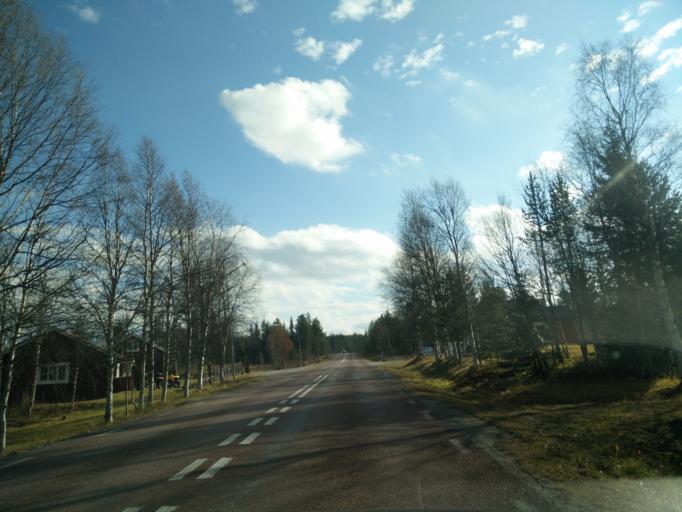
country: NO
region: Hedmark
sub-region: Engerdal
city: Engerdal
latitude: 62.5051
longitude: 12.6186
